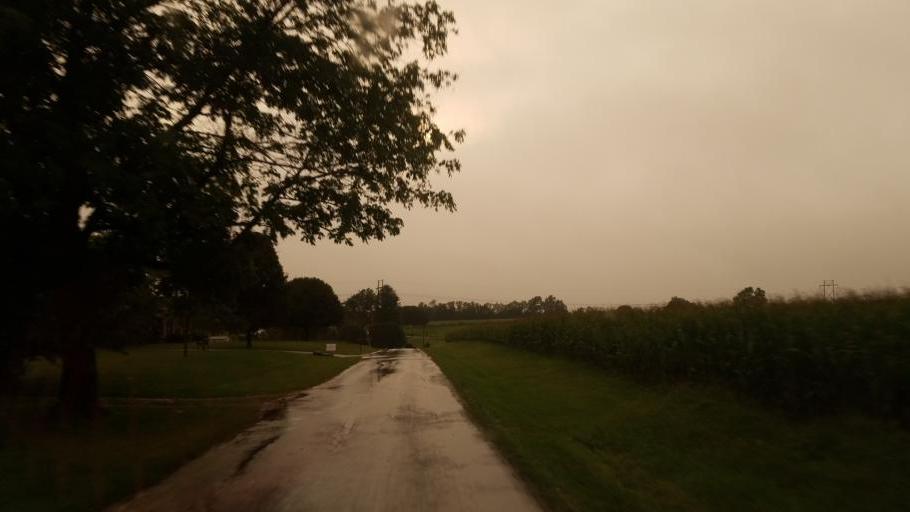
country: US
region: Kentucky
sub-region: Fleming County
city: Flemingsburg
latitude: 38.4681
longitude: -83.6349
